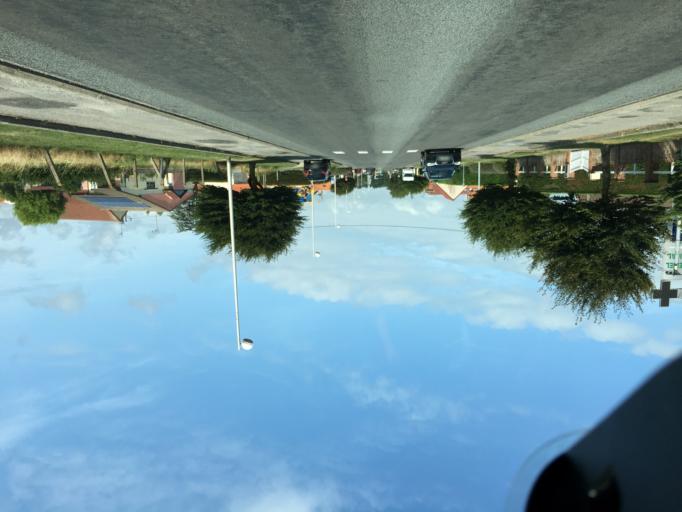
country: FR
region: Nord-Pas-de-Calais
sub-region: Departement du Pas-de-Calais
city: Berck-Plage
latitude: 50.4046
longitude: 1.5788
